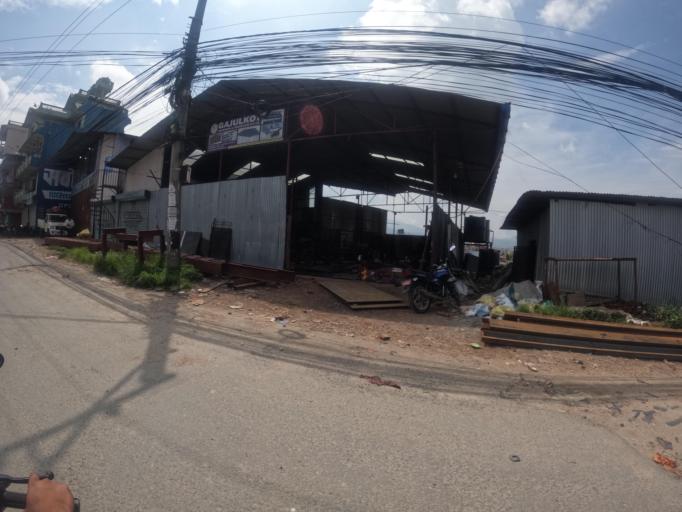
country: NP
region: Central Region
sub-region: Bagmati Zone
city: Patan
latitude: 27.6741
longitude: 85.3690
